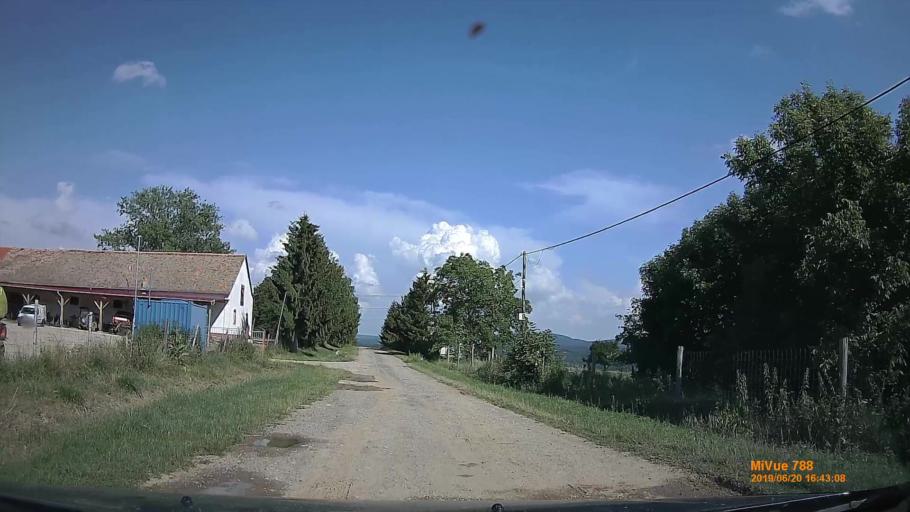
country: HU
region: Baranya
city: Buekkoesd
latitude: 46.1602
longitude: 18.0383
